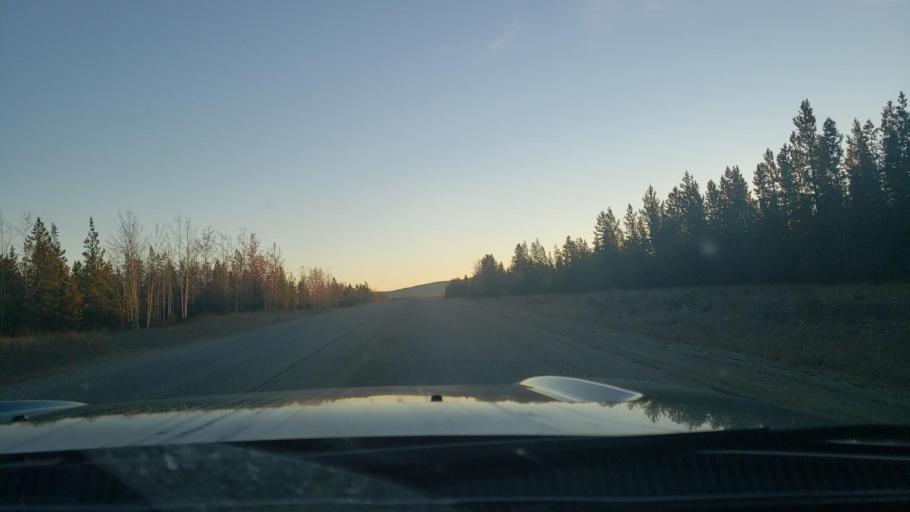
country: CA
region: Yukon
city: Watson Lake
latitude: 59.9338
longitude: -128.2546
